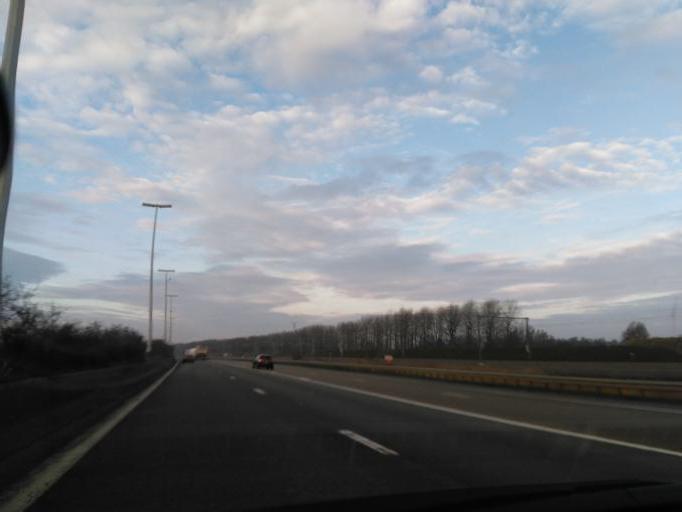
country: BE
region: Flanders
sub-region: Provincie Oost-Vlaanderen
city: Beveren
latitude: 51.2427
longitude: 4.2424
